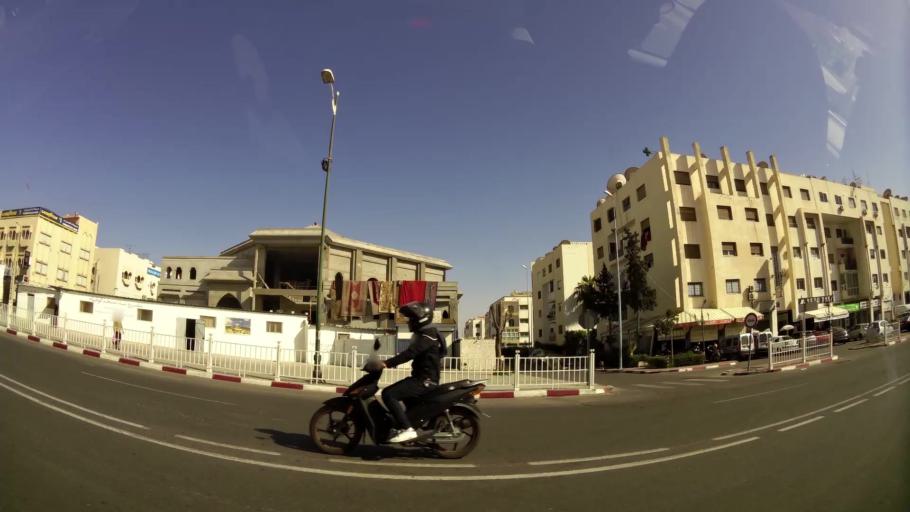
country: MA
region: Oued ed Dahab-Lagouira
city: Dakhla
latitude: 30.4198
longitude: -9.5617
